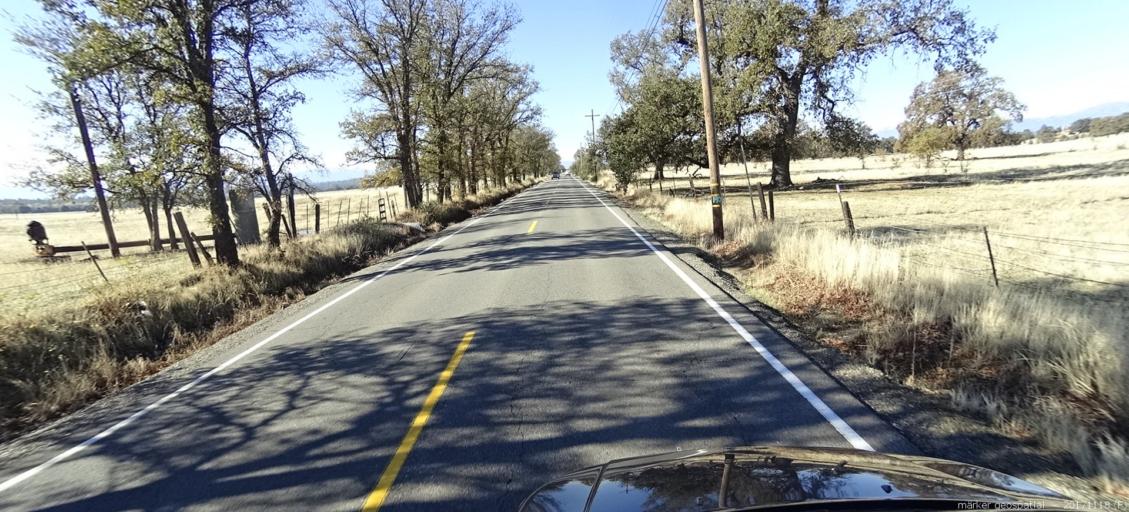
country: US
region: California
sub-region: Shasta County
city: Anderson
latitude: 40.3886
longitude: -122.3992
